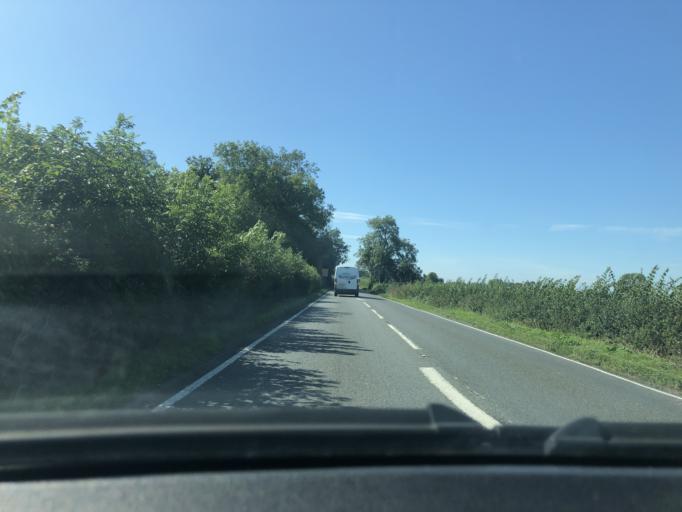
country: GB
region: England
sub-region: Somerset
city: Westonzoyland
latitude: 51.1366
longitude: -2.8601
